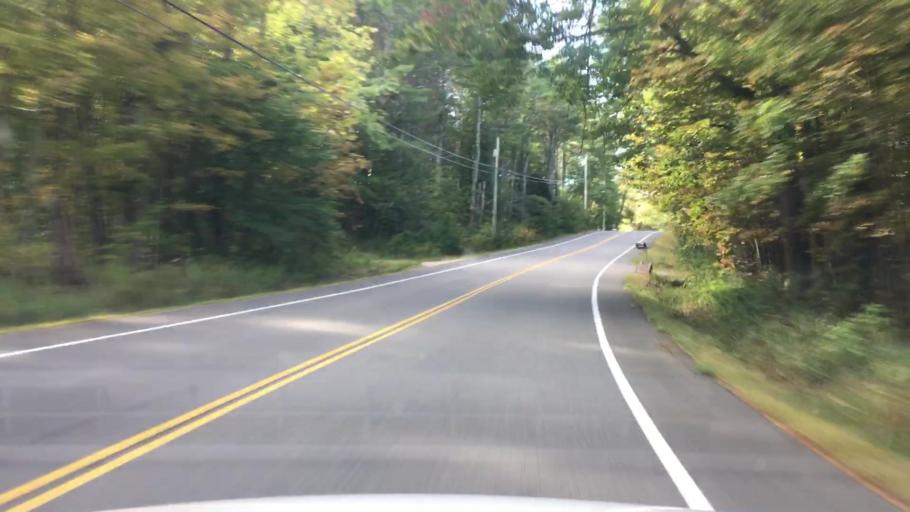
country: US
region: Maine
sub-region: Androscoggin County
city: Lisbon Falls
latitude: 43.9547
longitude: -70.0424
